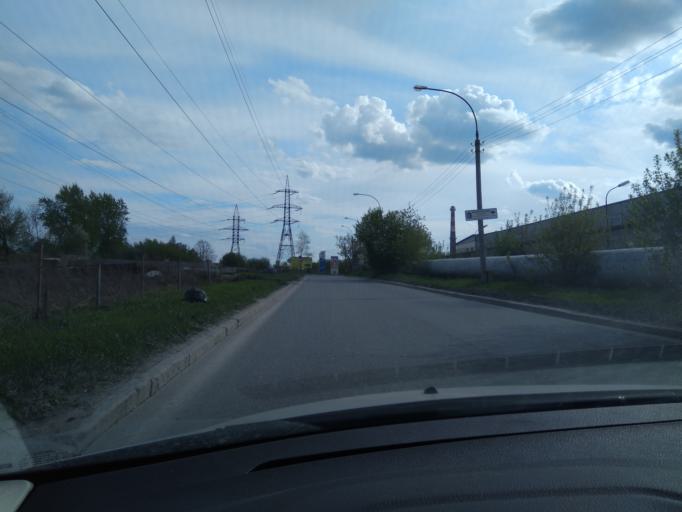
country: RU
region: Sverdlovsk
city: Yekaterinburg
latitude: 56.8833
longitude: 60.5518
